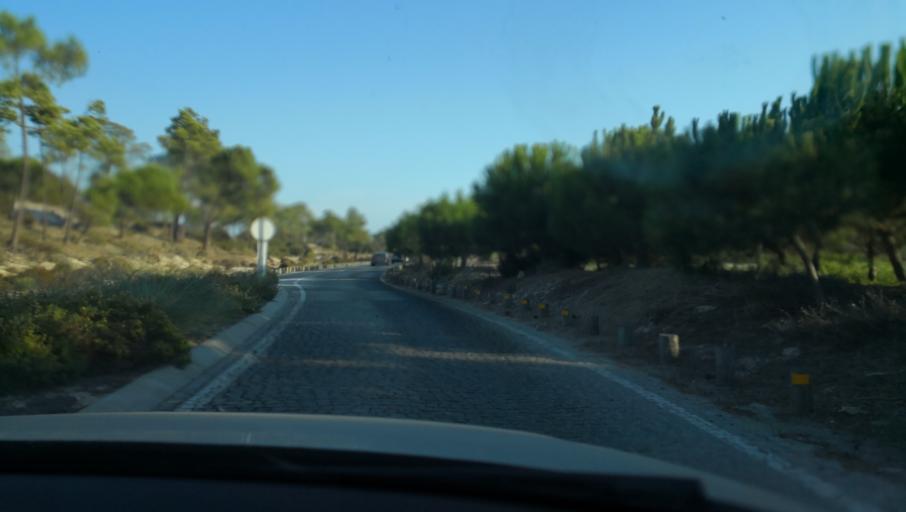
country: PT
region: Setubal
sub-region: Setubal
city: Setubal
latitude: 38.4813
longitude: -8.8912
